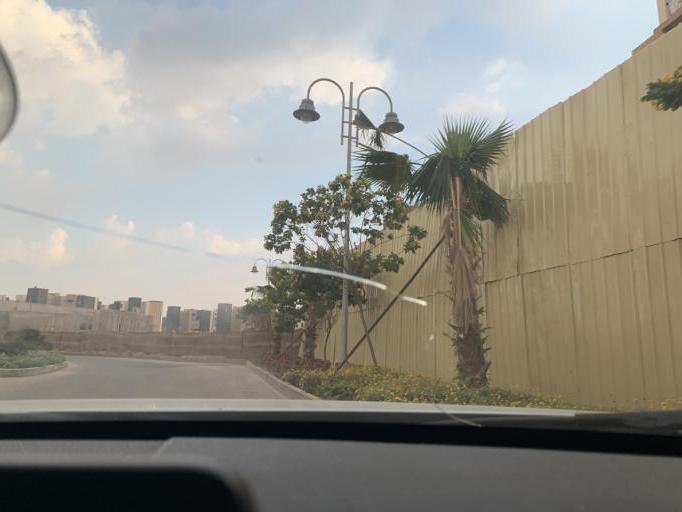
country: EG
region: Muhafazat al Qalyubiyah
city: Al Khankah
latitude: 30.1017
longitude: 31.6506
